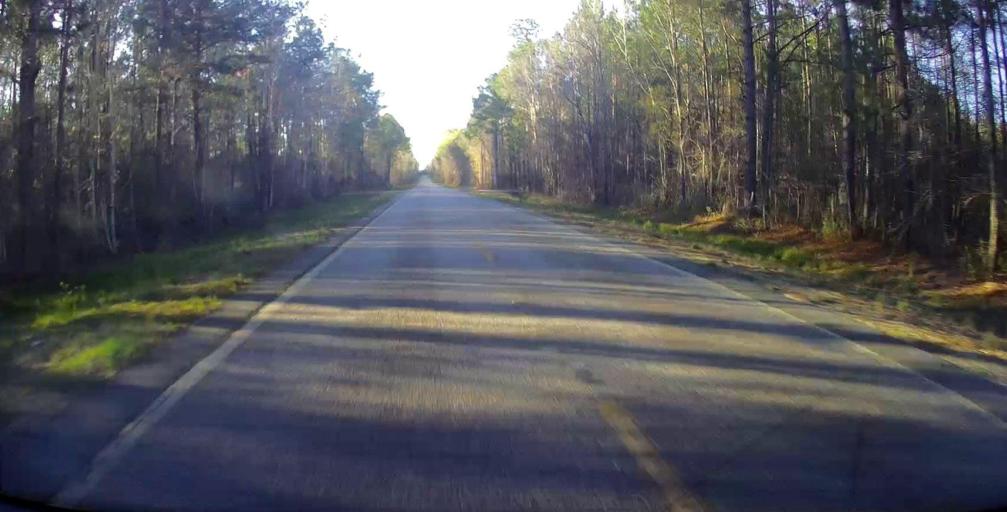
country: US
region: Georgia
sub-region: Wilcox County
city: Abbeville
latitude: 32.0938
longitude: -83.2981
